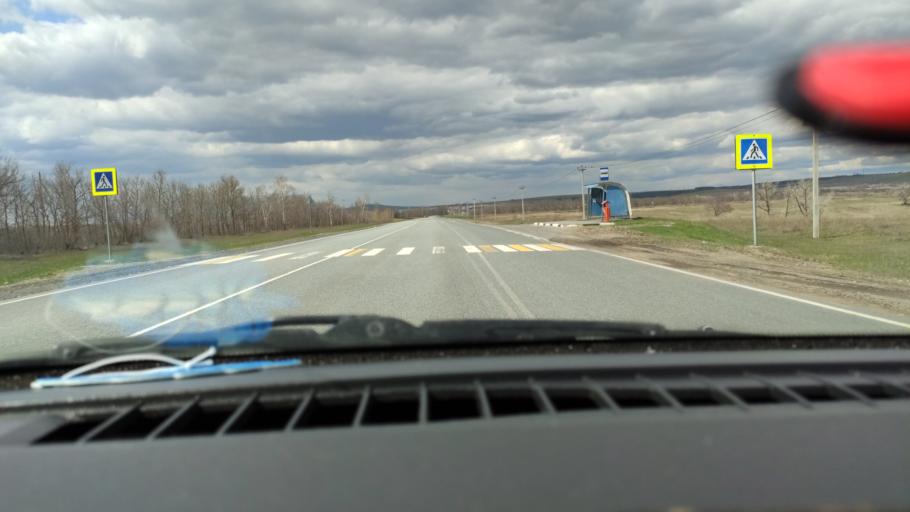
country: RU
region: Saratov
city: Tersa
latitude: 52.0856
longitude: 47.6206
